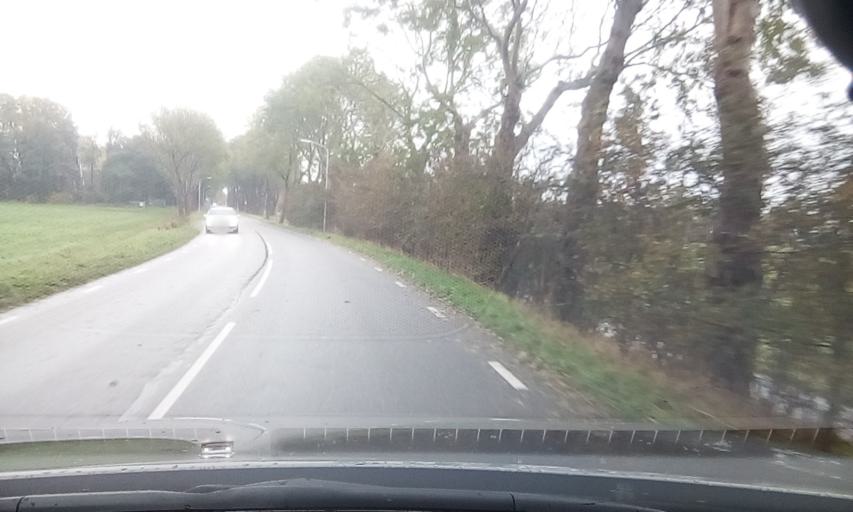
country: NL
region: Groningen
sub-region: Gemeente Haren
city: Haren
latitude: 53.2127
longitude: 6.6545
